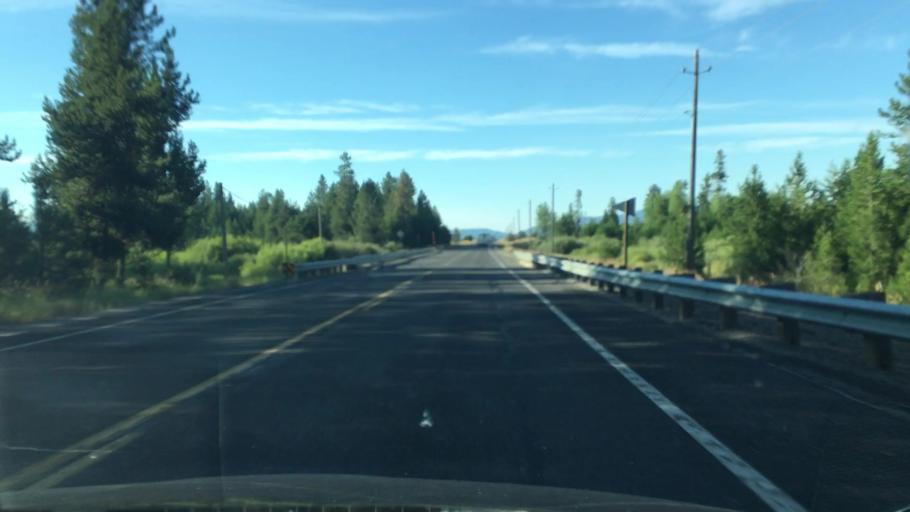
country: US
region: Idaho
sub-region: Valley County
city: Cascade
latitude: 44.4111
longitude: -115.9997
